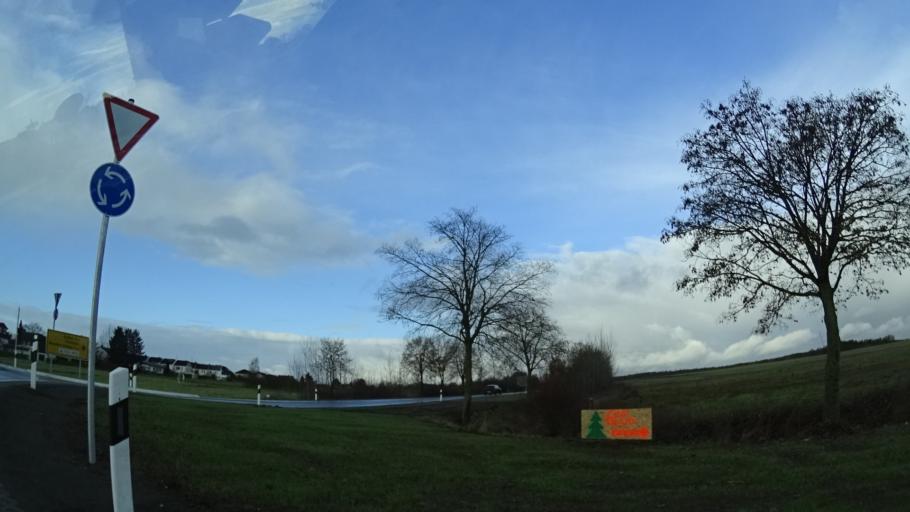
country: DE
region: Hesse
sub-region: Regierungsbezirk Giessen
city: Lich
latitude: 50.5409
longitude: 8.7539
